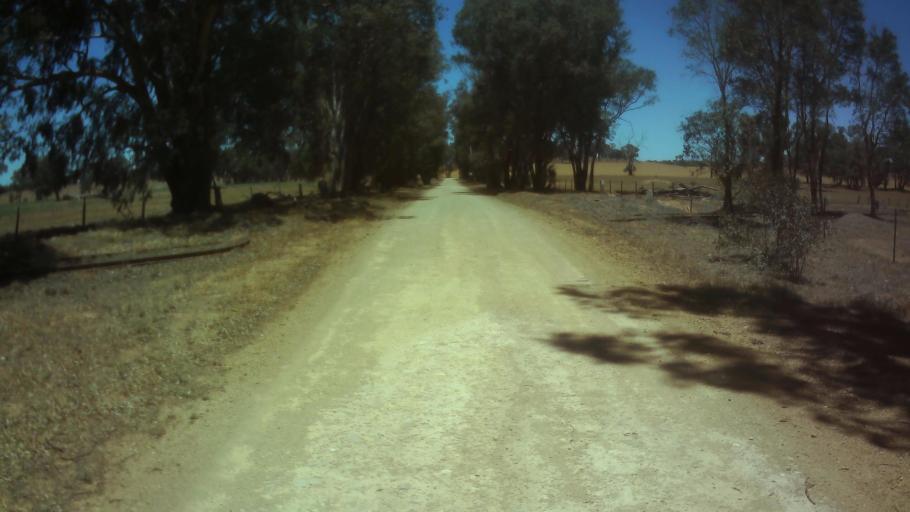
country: AU
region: New South Wales
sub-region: Weddin
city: Grenfell
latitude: -33.9189
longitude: 148.2127
